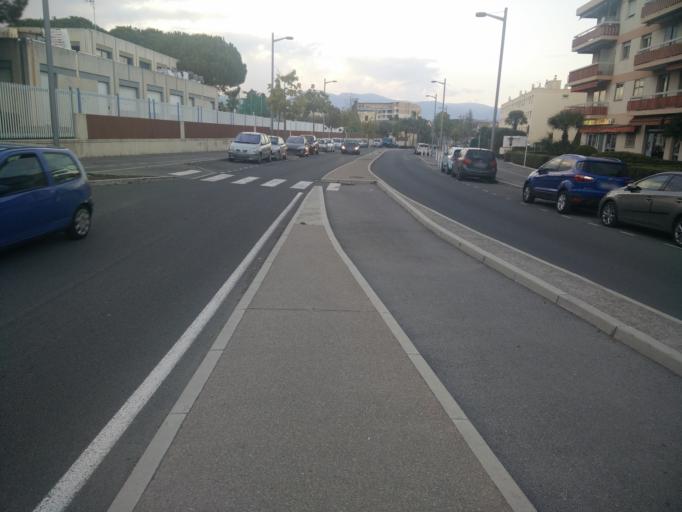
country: FR
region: Provence-Alpes-Cote d'Azur
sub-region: Departement des Alpes-Maritimes
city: Antibes
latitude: 43.5927
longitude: 7.1154
